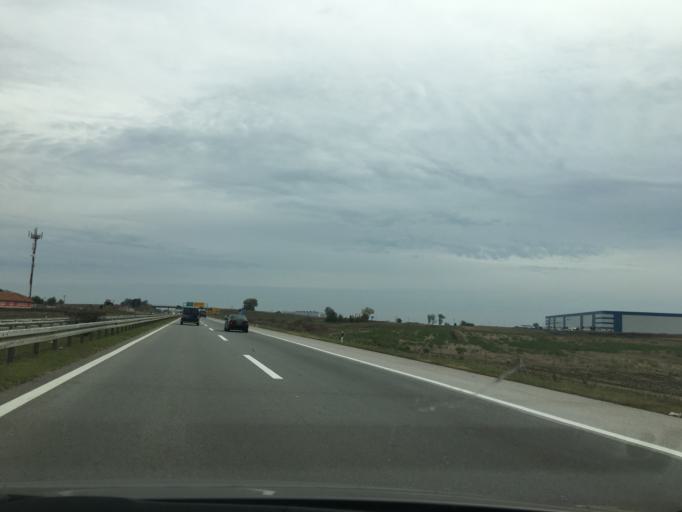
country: RS
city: Novi Banovci
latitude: 44.9467
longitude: 20.2757
